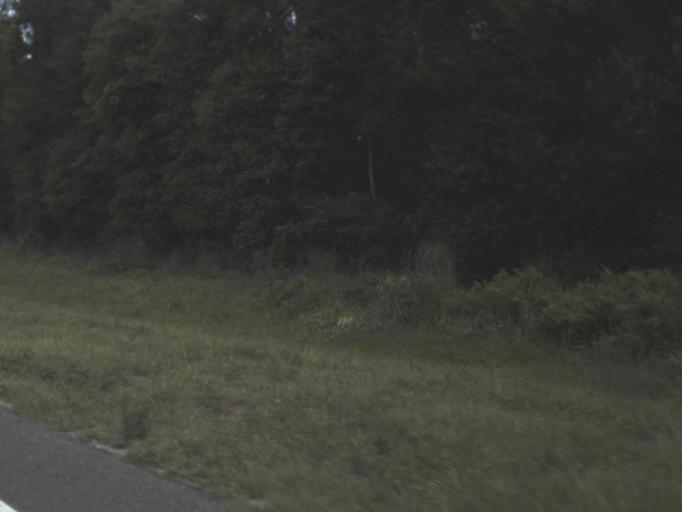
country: US
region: Florida
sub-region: Taylor County
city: Perry
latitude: 30.0325
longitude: -83.5426
